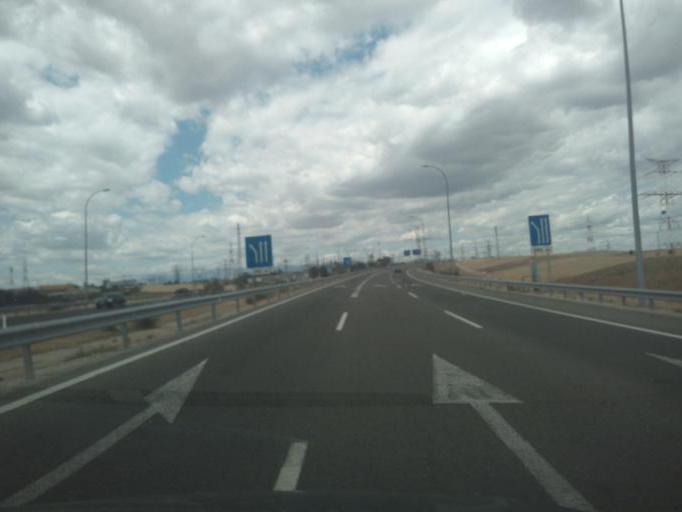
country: ES
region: Madrid
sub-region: Provincia de Madrid
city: San Sebastian de los Reyes
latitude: 40.5574
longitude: -3.5890
